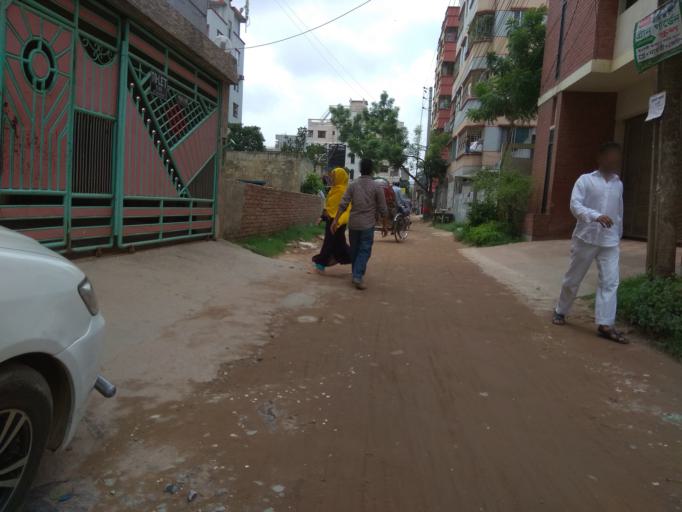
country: BD
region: Dhaka
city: Tungi
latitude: 23.8243
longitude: 90.3538
